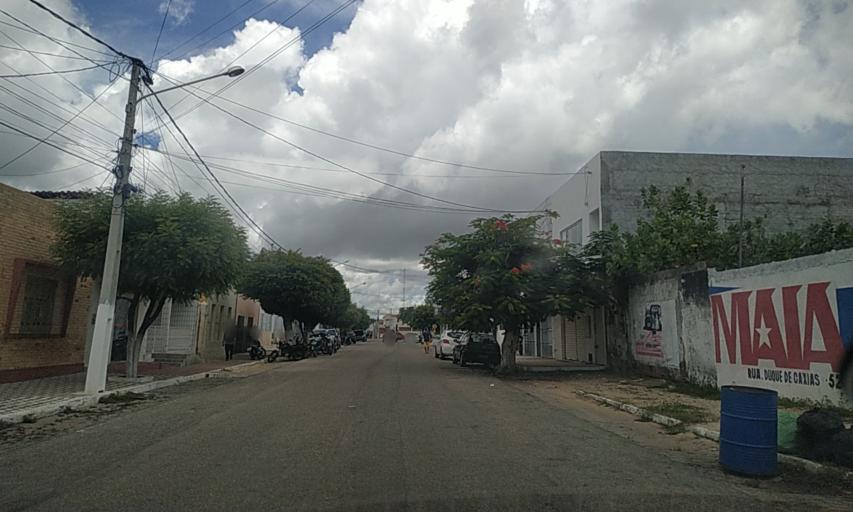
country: BR
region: Rio Grande do Norte
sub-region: Areia Branca
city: Areia Branca
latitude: -4.9552
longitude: -37.1357
